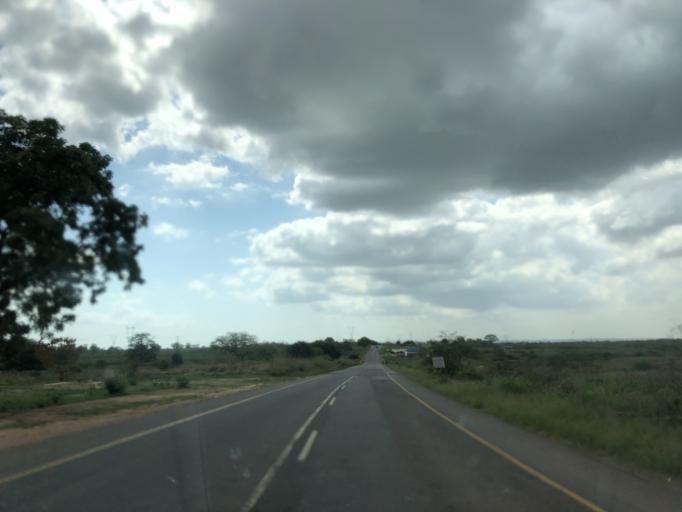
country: AO
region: Bengo
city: Caxito
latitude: -9.1186
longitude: 13.7331
